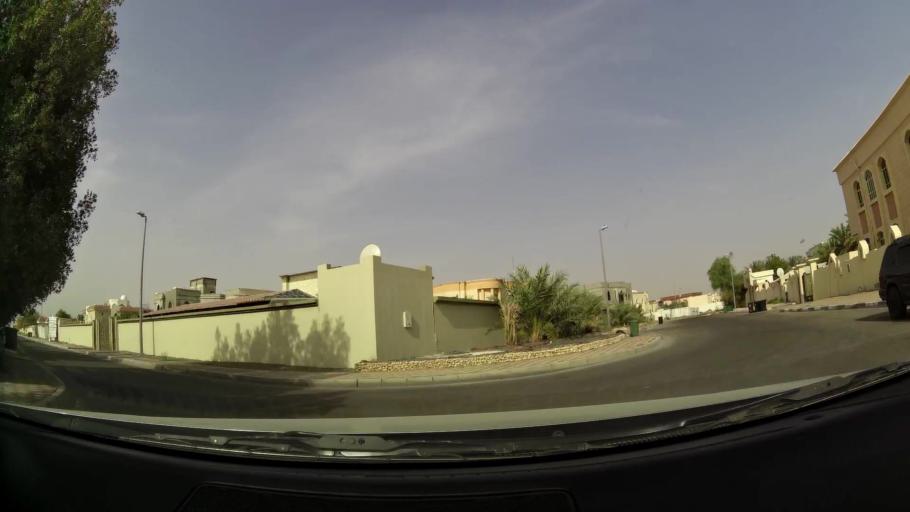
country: AE
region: Abu Dhabi
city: Al Ain
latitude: 24.1354
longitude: 55.7078
